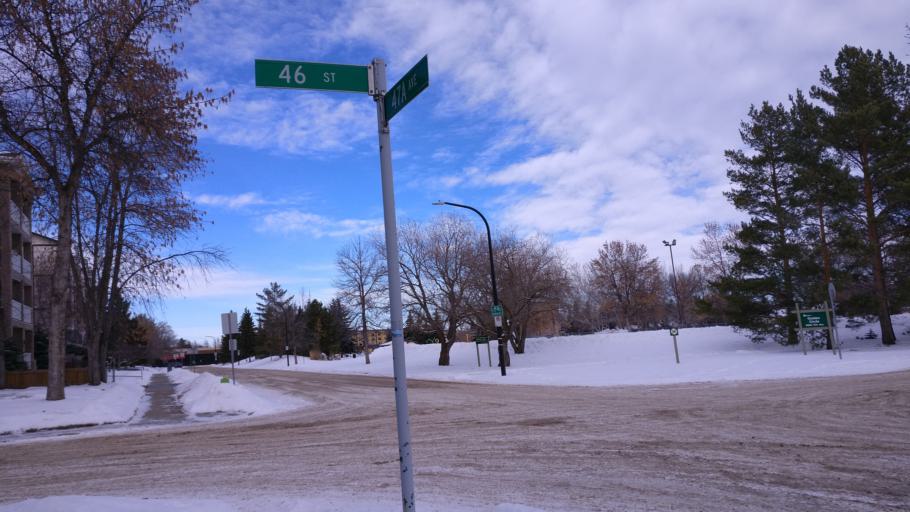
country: CA
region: Alberta
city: Red Deer
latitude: 52.2651
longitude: -113.8076
